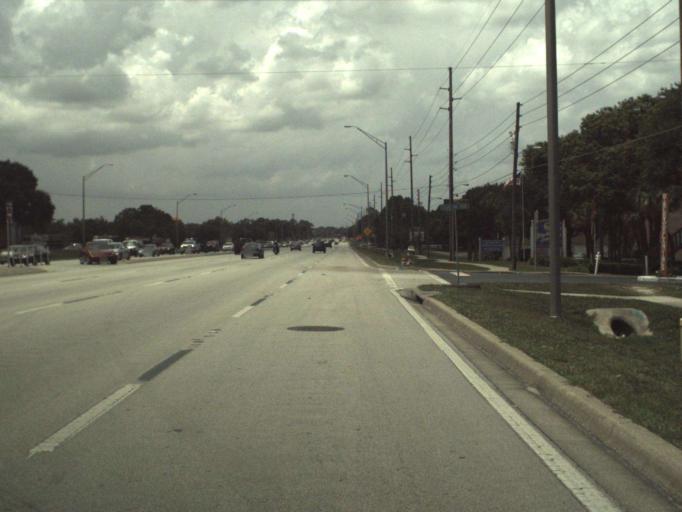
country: US
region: Florida
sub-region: Seminole County
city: Goldenrod
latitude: 28.6273
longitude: -81.3166
